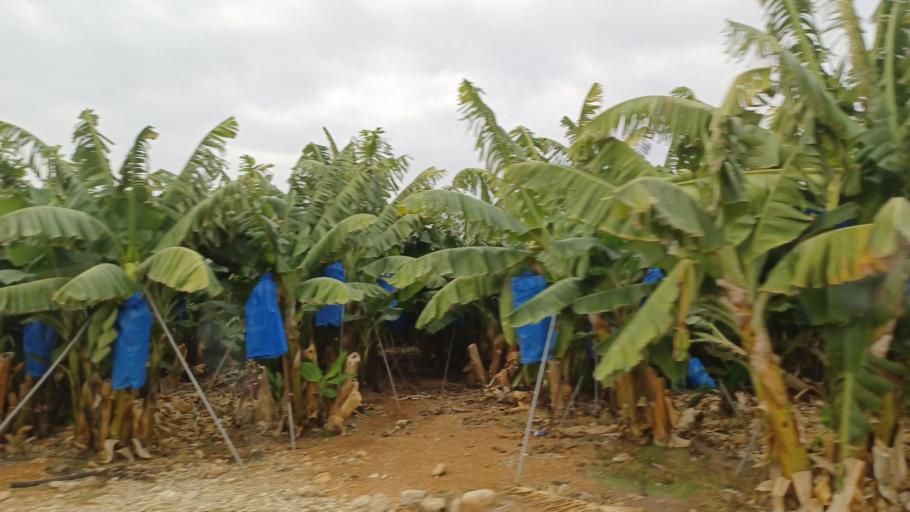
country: CY
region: Pafos
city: Pegeia
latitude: 34.8931
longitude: 32.3367
